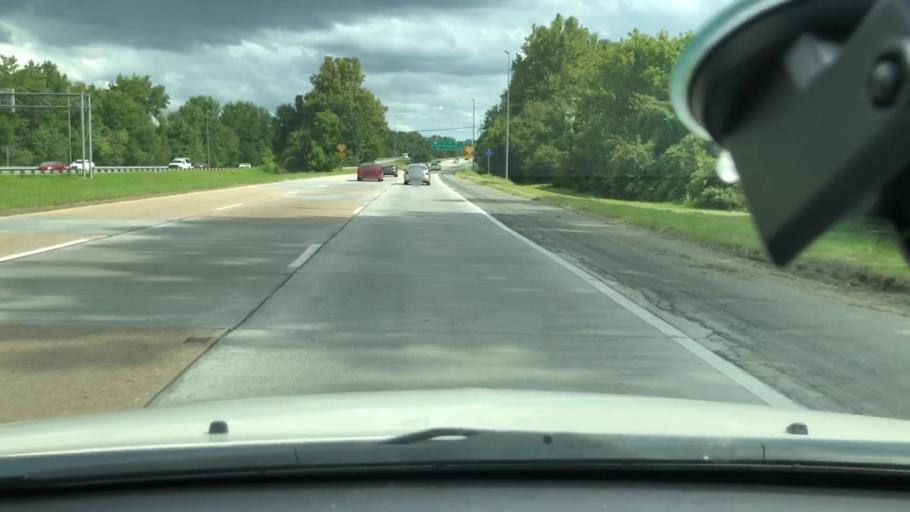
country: US
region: Virginia
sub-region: City of Chesapeake
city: Chesapeake
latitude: 36.7689
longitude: -76.2724
